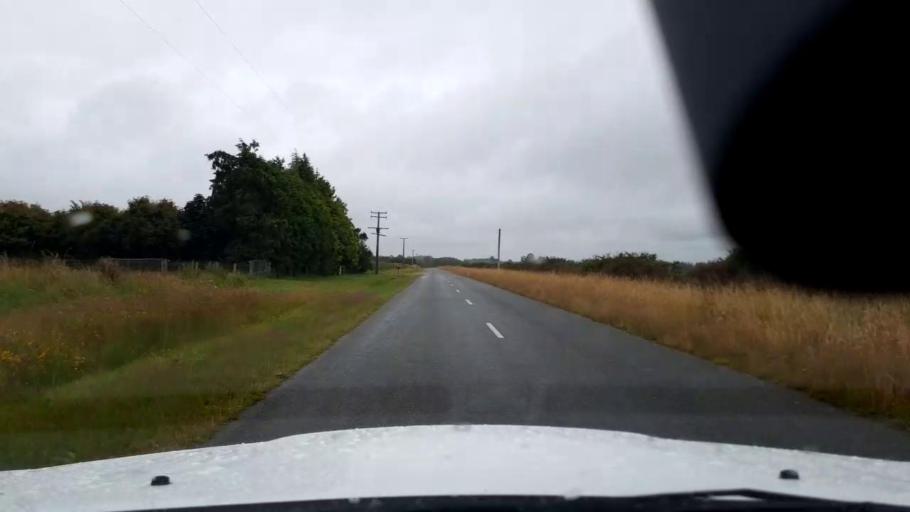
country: NZ
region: Canterbury
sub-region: Timaru District
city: Pleasant Point
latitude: -44.2539
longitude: 171.2441
